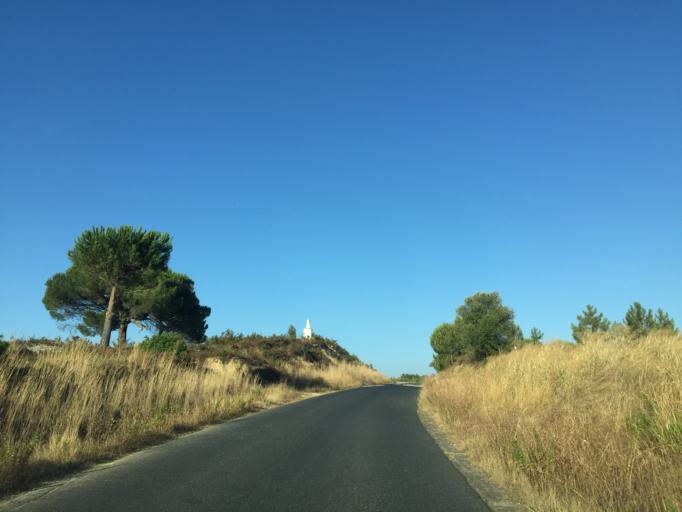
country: PT
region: Lisbon
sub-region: Azambuja
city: Aveiras de Cima
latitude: 39.1359
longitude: -8.9343
